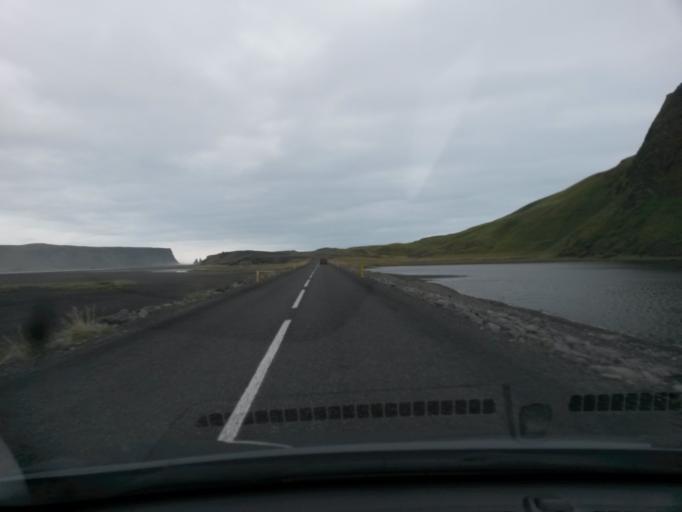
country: IS
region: South
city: Vestmannaeyjar
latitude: 63.4112
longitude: -19.1289
